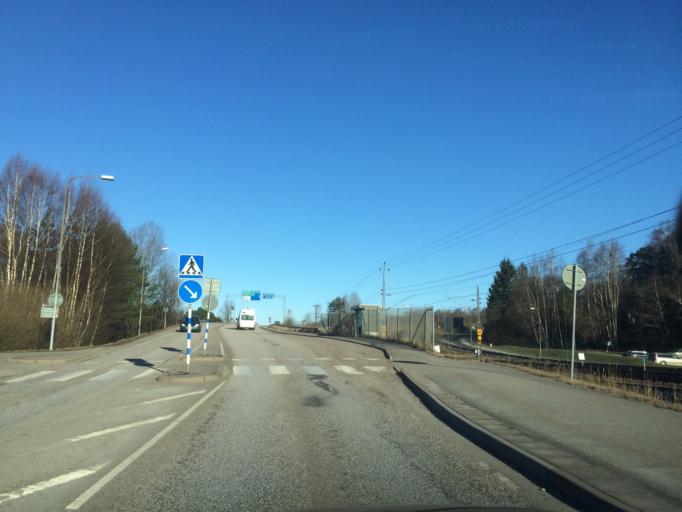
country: SE
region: Vaestra Goetaland
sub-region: Molndal
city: Kallered
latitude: 57.5995
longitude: 12.0581
